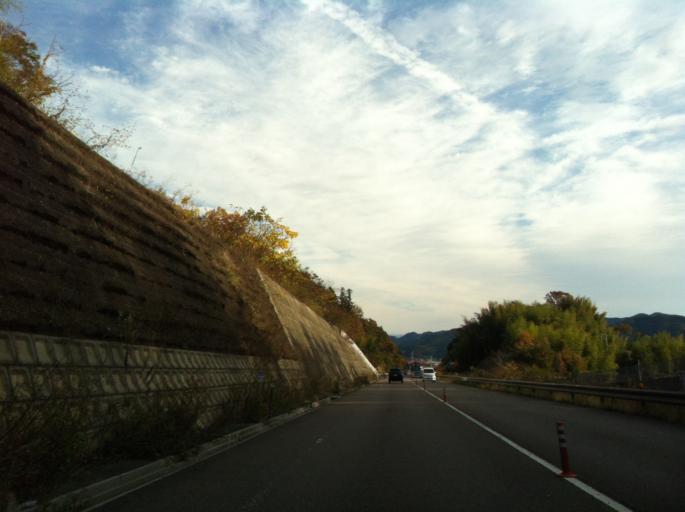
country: JP
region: Gifu
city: Minokamo
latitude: 35.4837
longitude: 137.0506
